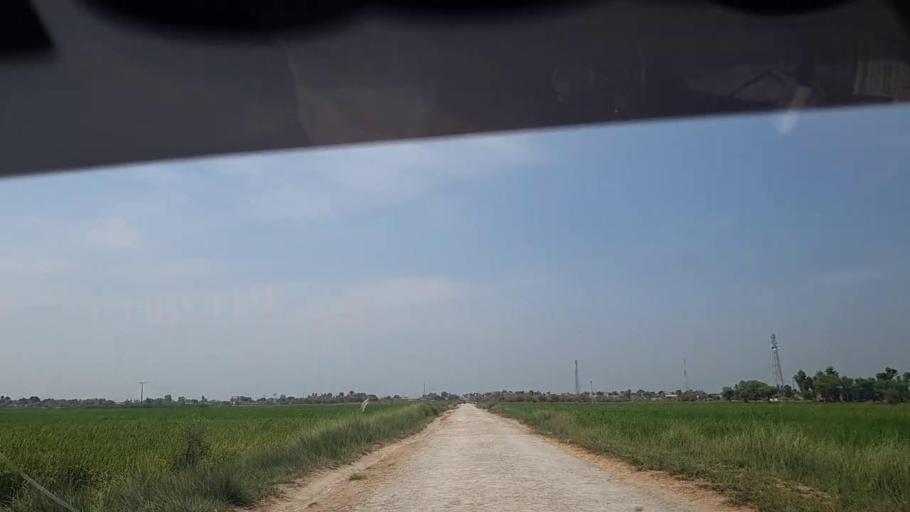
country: PK
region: Sindh
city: Thul
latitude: 28.1762
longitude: 68.7363
